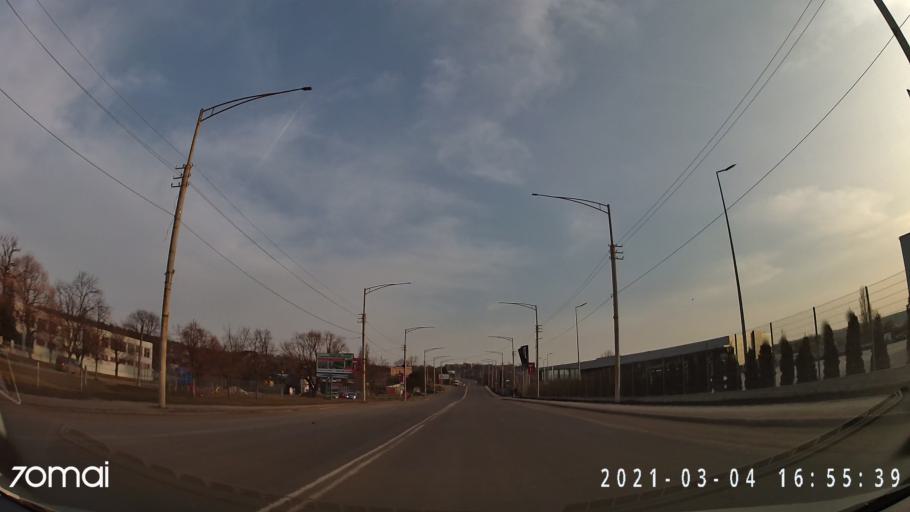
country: MD
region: Balti
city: Balti
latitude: 47.7548
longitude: 27.9420
